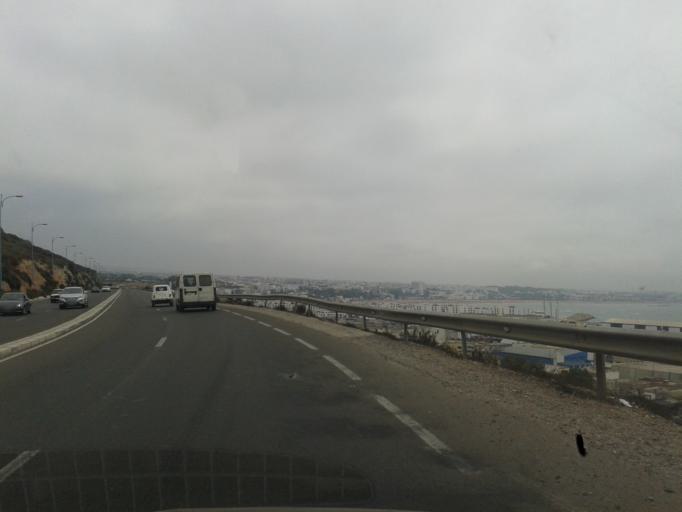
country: MA
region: Souss-Massa-Draa
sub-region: Agadir-Ida-ou-Tnan
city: Agadir
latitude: 30.4263
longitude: -9.6296
